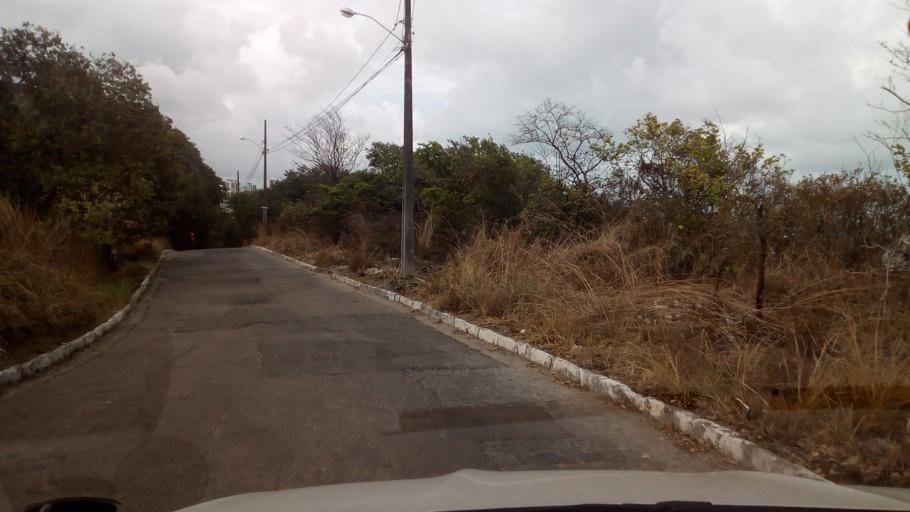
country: BR
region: Paraiba
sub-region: Joao Pessoa
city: Joao Pessoa
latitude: -7.1348
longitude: -34.8226
